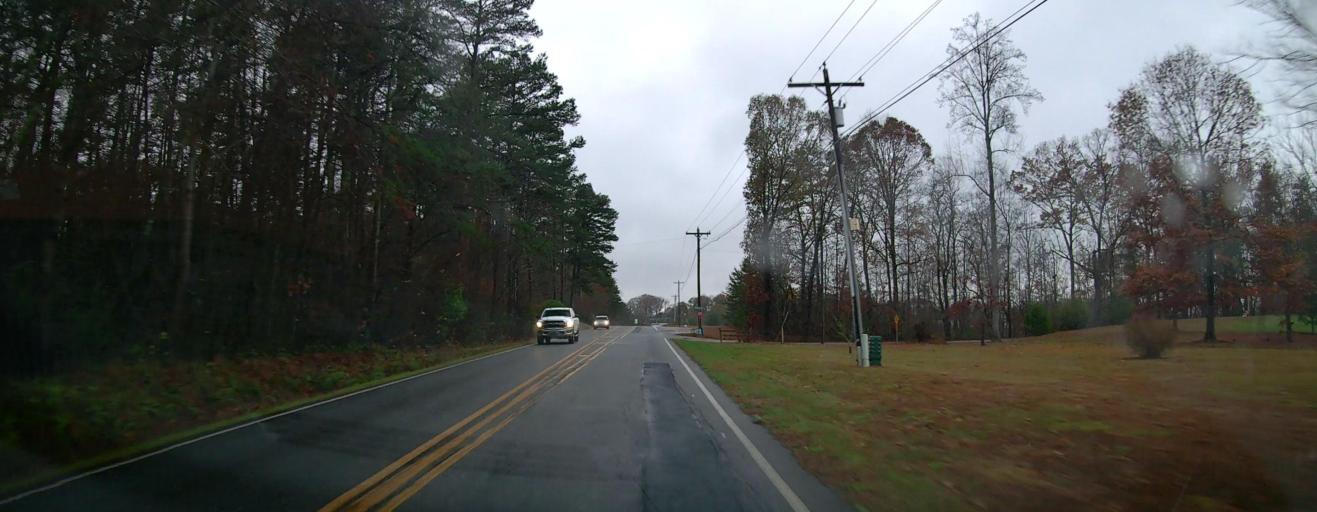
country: US
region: Georgia
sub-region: Habersham County
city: Cornelia
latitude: 34.5195
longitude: -83.5652
